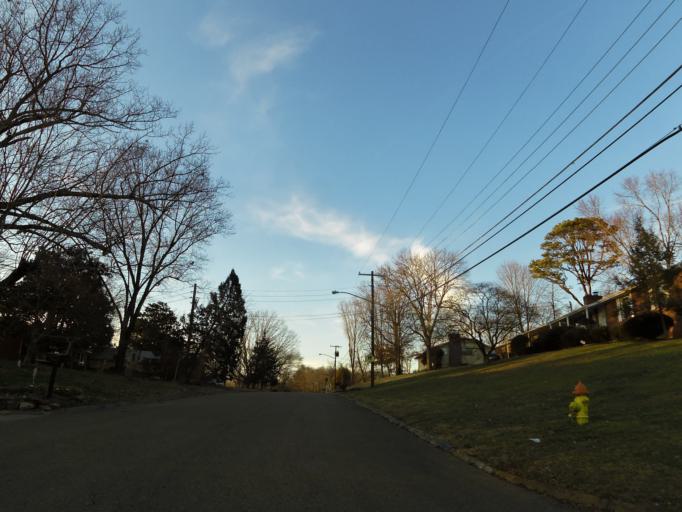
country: US
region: Tennessee
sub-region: Knox County
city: Knoxville
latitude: 36.0165
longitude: -83.8736
